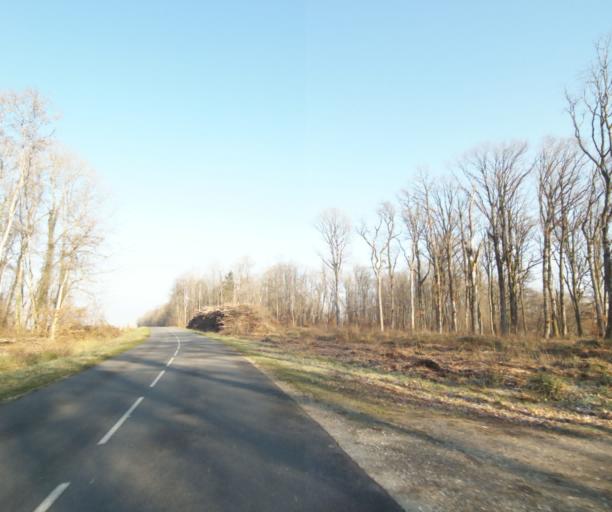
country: FR
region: Champagne-Ardenne
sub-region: Departement de la Haute-Marne
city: Wassy
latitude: 48.4810
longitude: 4.9341
